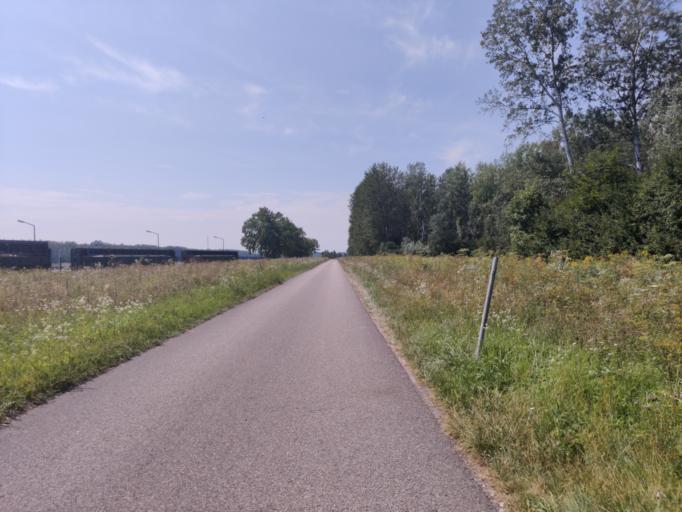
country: AT
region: Upper Austria
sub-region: Politischer Bezirk Urfahr-Umgebung
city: Ottensheim
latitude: 48.3185
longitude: 14.1458
